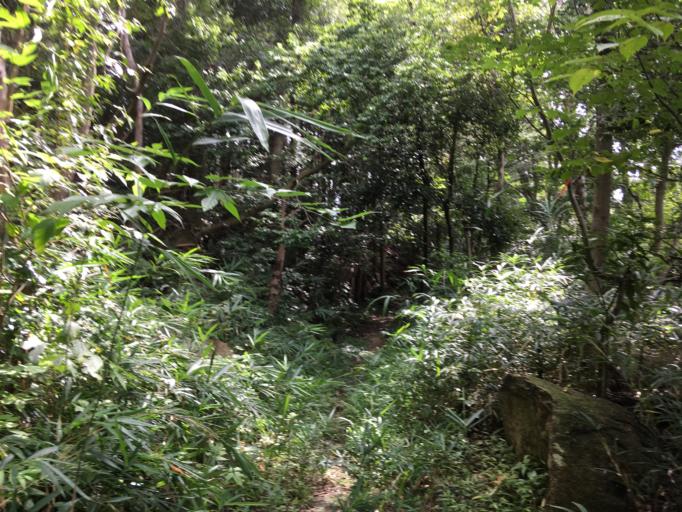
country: JP
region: Nara
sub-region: Ikoma-shi
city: Ikoma
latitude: 34.7013
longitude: 135.6639
